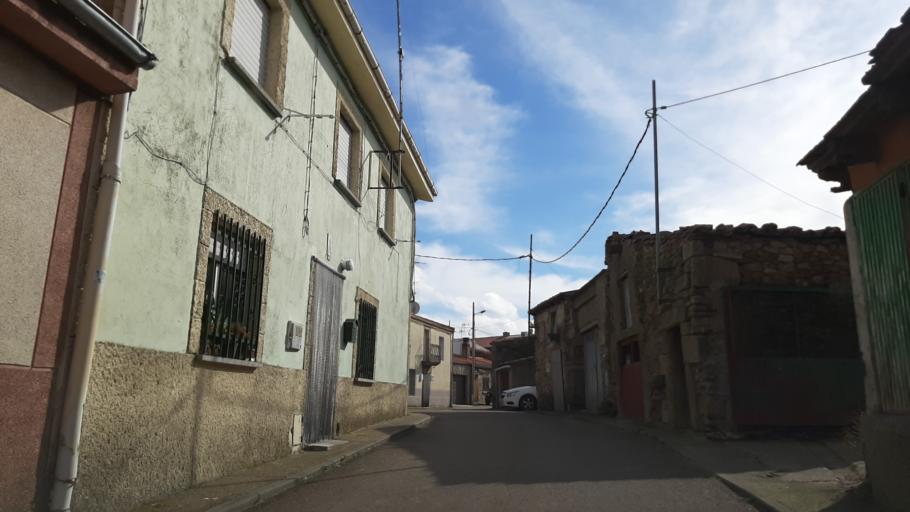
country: ES
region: Castille and Leon
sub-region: Provincia de Salamanca
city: Villarino de los Aires
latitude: 41.2420
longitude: -6.5234
